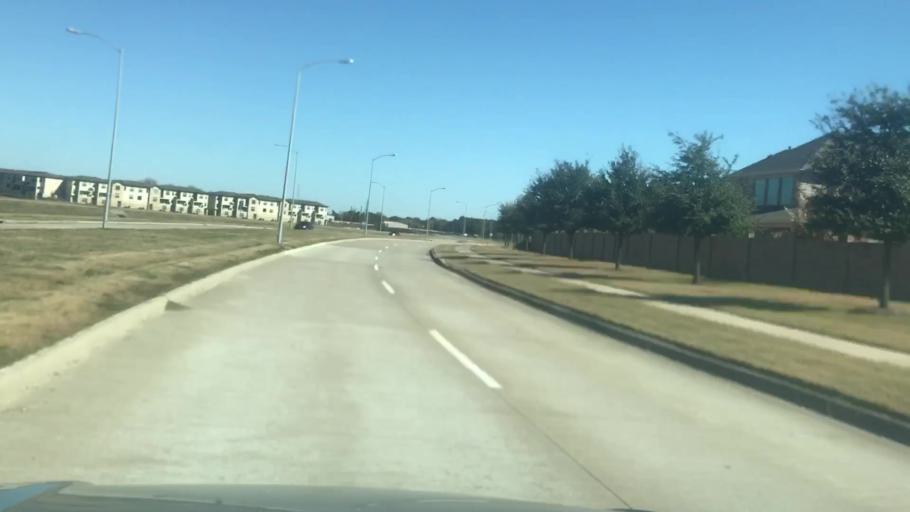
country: US
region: Texas
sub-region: Fort Bend County
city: Cinco Ranch
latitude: 29.7362
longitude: -95.8020
